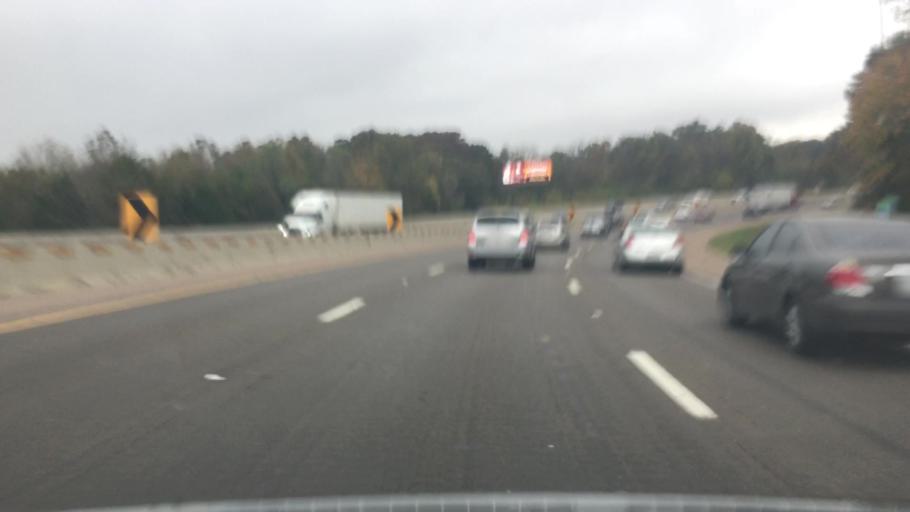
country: US
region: Mississippi
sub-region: Rankin County
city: Flowood
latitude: 32.3168
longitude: -90.1584
